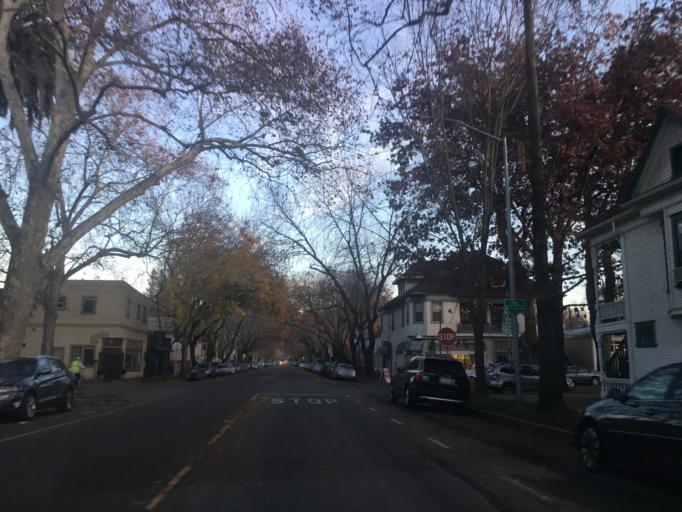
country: US
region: California
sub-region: Sacramento County
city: Sacramento
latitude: 38.5691
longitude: -121.4973
